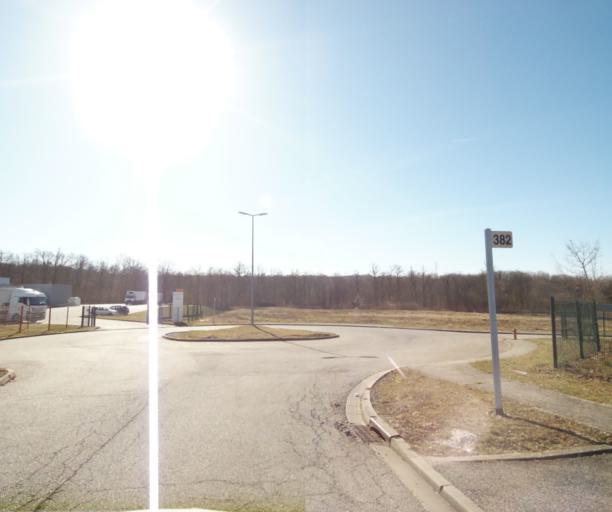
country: FR
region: Lorraine
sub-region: Departement de Meurthe-et-Moselle
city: Richardmenil
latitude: 48.6098
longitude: 6.1817
